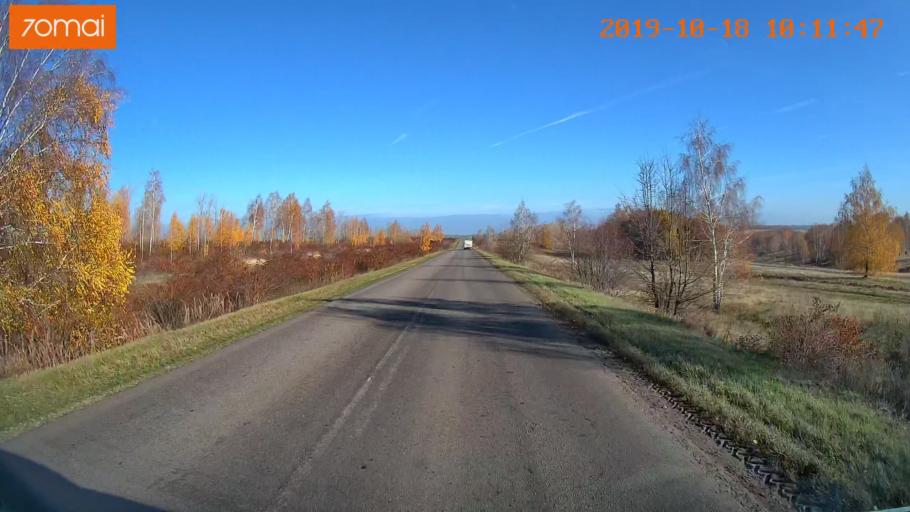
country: RU
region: Tula
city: Kurkino
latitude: 53.3860
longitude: 38.5026
